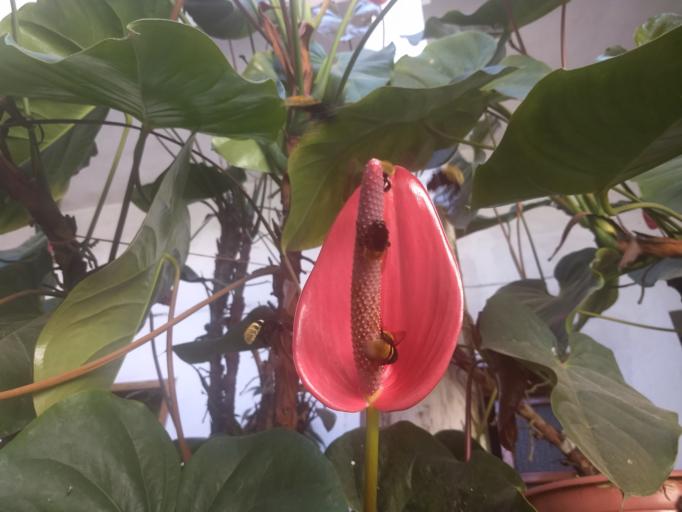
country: MX
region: Puebla
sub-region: Cuetzalan del Progreso
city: Ciudad de Cuetzalan
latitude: 20.0181
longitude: -97.5208
